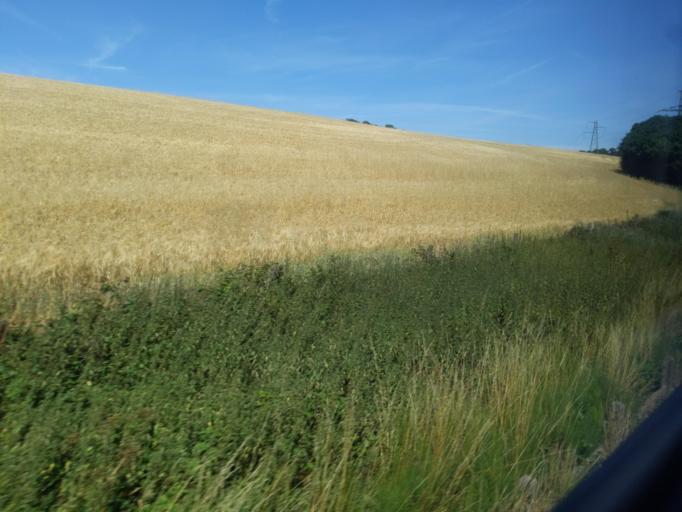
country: GB
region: England
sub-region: Devon
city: Ipplepen
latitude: 50.4733
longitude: -3.6498
